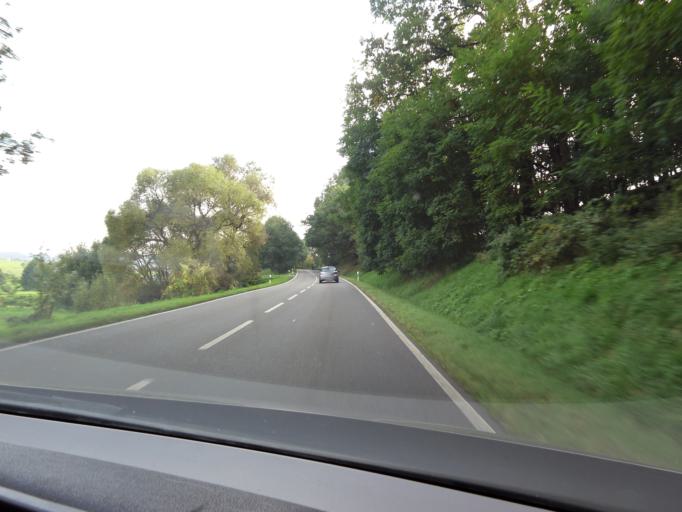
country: DE
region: Thuringia
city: Fambach
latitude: 50.7486
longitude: 10.3603
